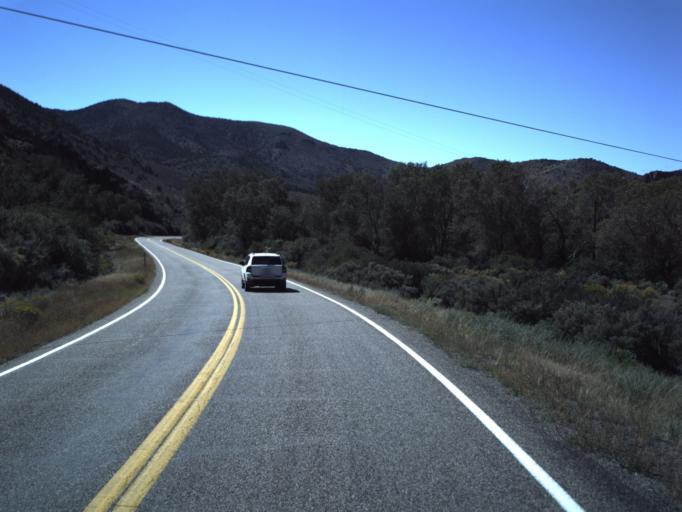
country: US
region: Utah
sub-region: Piute County
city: Junction
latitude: 38.2034
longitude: -112.1629
